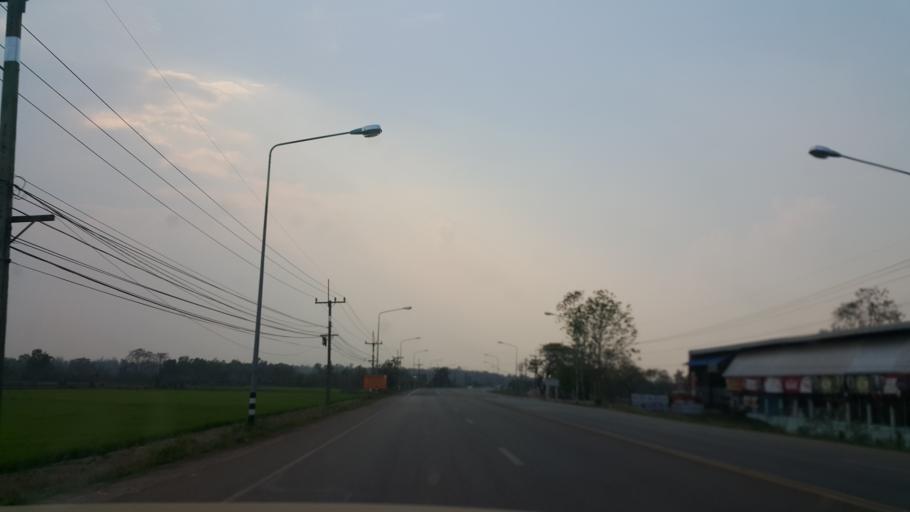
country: TH
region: Nakhon Phanom
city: Renu Nakhon
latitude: 17.0214
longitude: 104.7215
